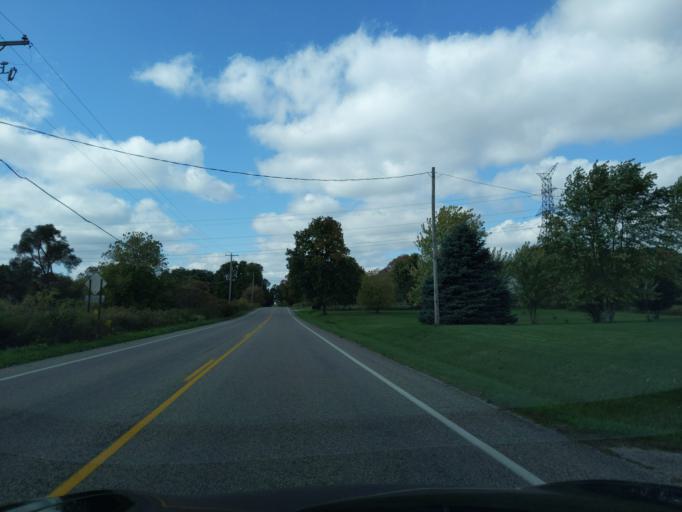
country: US
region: Michigan
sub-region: Eaton County
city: Charlotte
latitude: 42.5676
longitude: -84.7703
